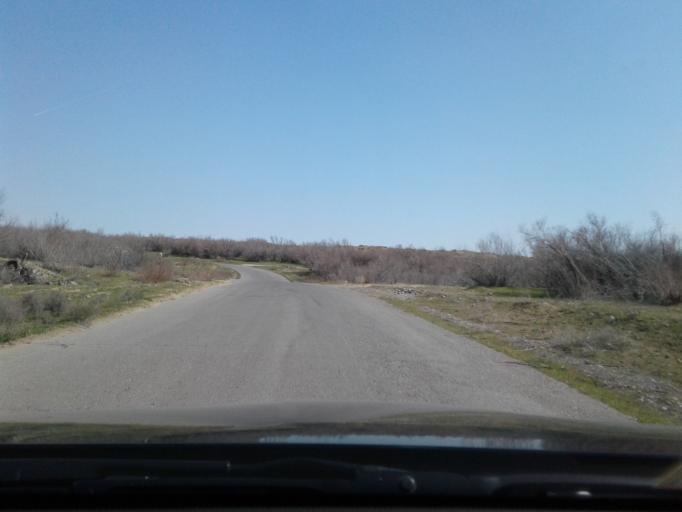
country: TM
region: Ahal
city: Abadan
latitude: 38.1470
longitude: 58.1962
